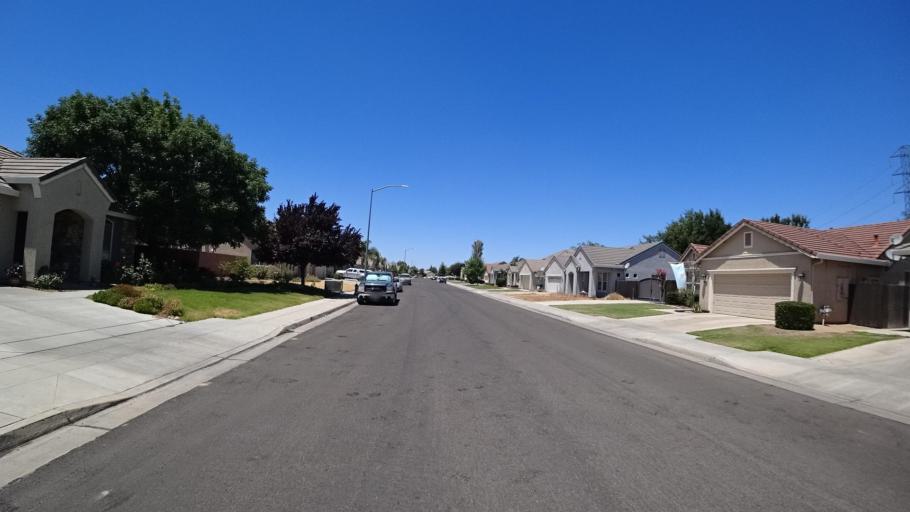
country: US
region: California
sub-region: Fresno County
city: Sunnyside
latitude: 36.7336
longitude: -119.6651
